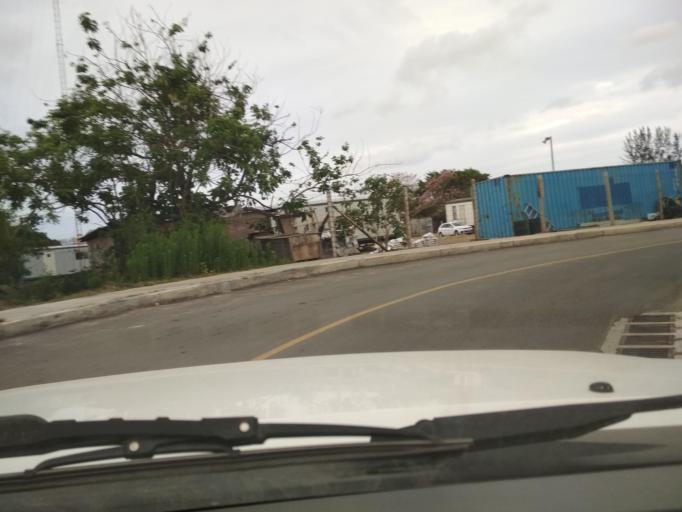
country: MX
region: Veracruz
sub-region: Medellin
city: Fraccionamiento Arboledas San Ramon
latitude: 19.0803
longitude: -96.1373
